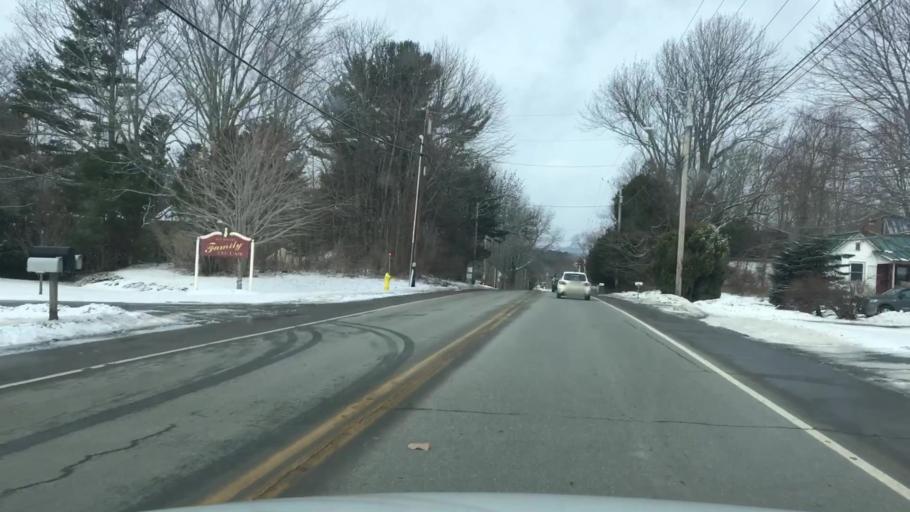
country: US
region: Maine
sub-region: Knox County
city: Rockport
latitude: 44.1750
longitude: -69.0796
